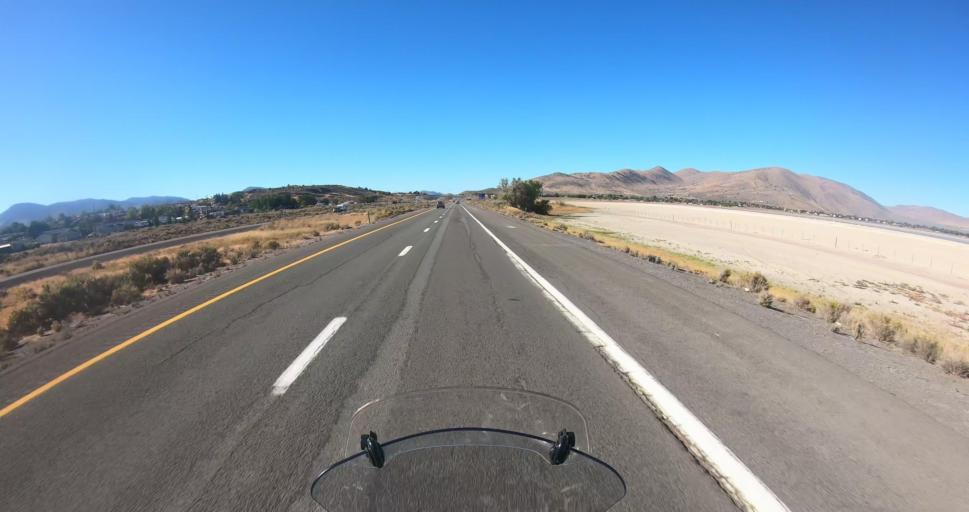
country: US
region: Nevada
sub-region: Washoe County
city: Cold Springs
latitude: 39.6585
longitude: -119.9880
